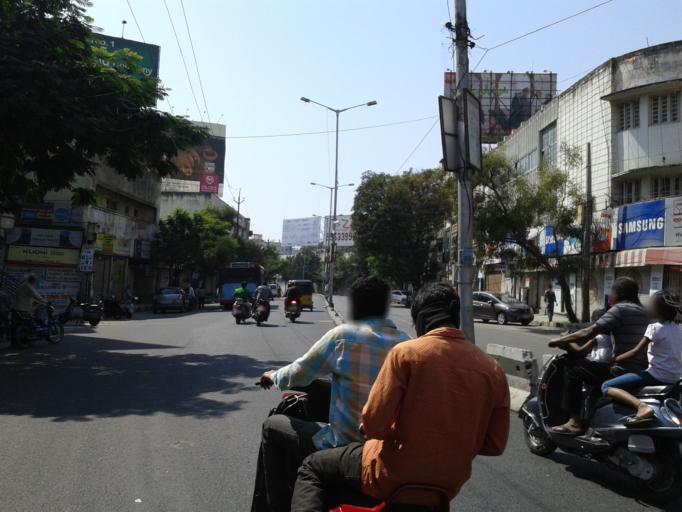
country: IN
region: Telangana
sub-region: Hyderabad
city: Malkajgiri
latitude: 17.4384
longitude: 78.4949
